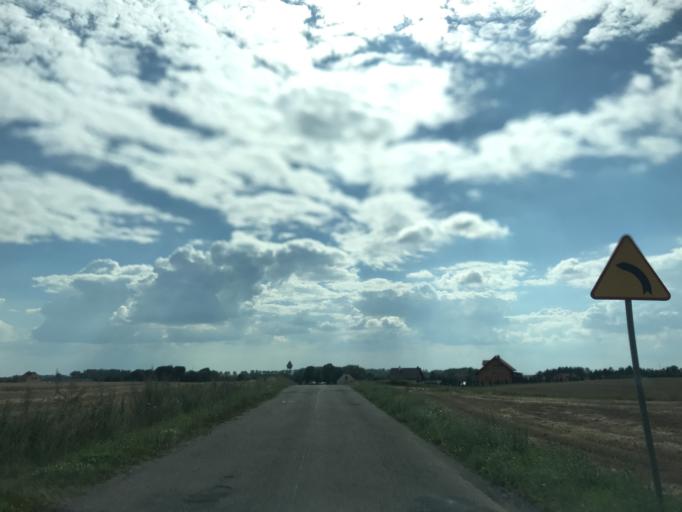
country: PL
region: Kujawsko-Pomorskie
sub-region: Powiat brodnicki
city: Brzozie
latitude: 53.3361
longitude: 19.6602
